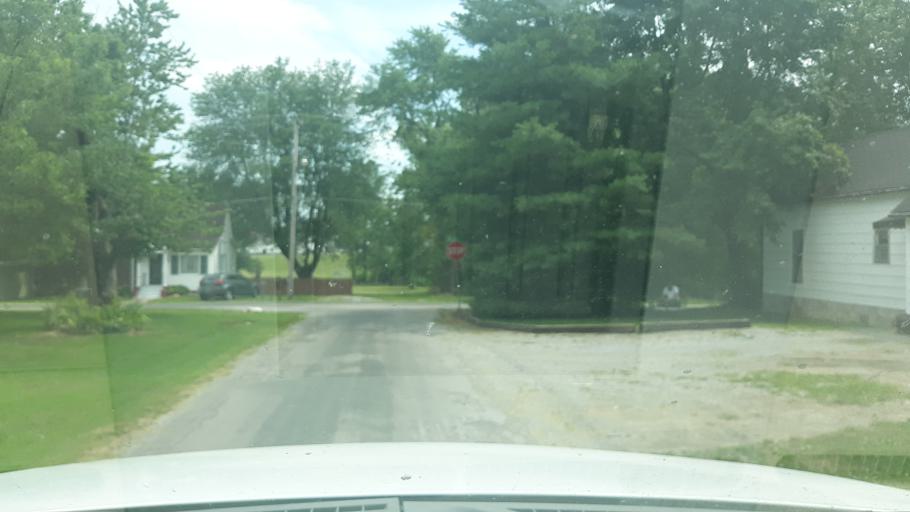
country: US
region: Illinois
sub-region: Saline County
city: Harrisburg
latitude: 37.8436
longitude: -88.6116
